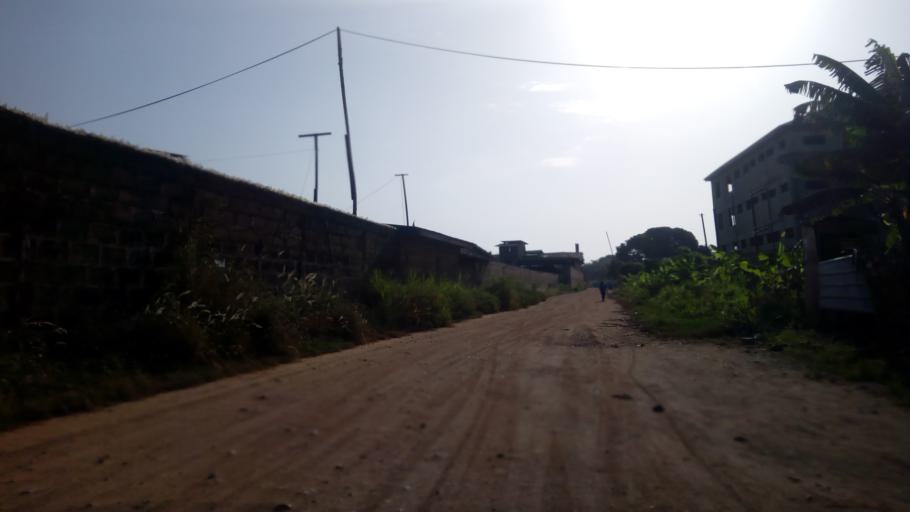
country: GH
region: Central
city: Cape Coast
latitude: 5.1148
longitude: -1.2785
